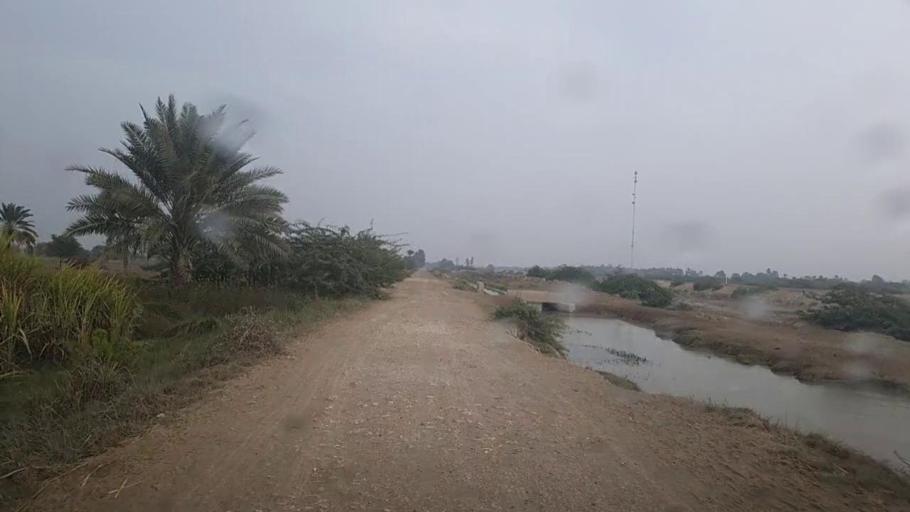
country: PK
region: Sindh
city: Gambat
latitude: 27.3816
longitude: 68.5817
